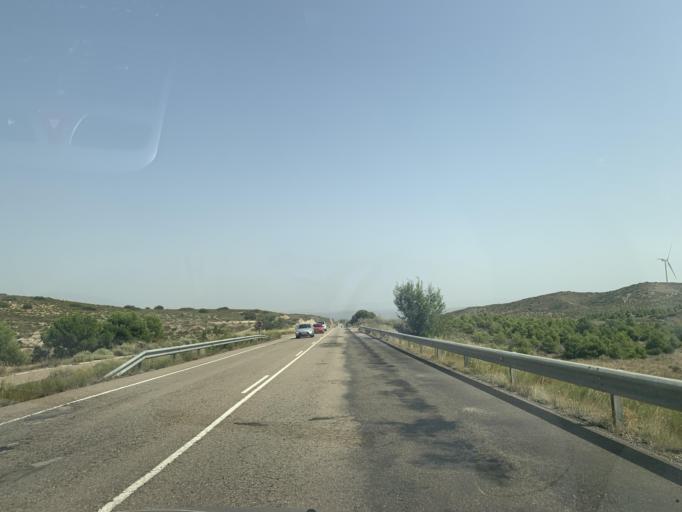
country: ES
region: Aragon
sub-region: Provincia de Zaragoza
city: El Burgo de Ebro
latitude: 41.5050
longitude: -0.7109
